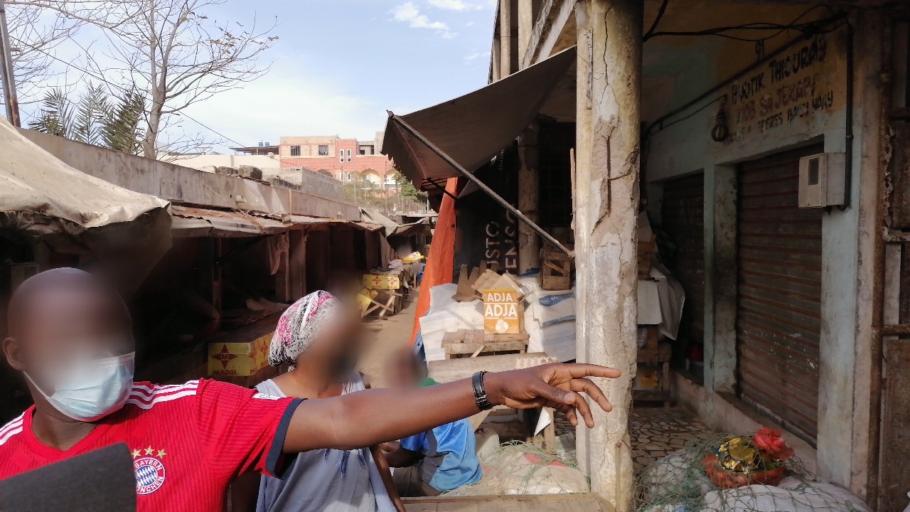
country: SN
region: Dakar
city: Pikine
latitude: 14.7808
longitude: -17.3896
